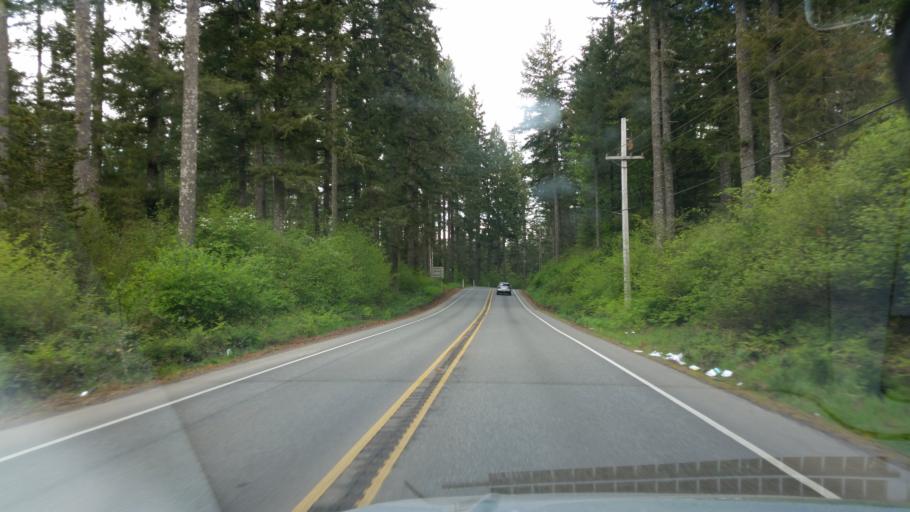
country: US
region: Washington
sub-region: Mason County
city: Allyn
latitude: 47.4112
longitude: -122.8420
